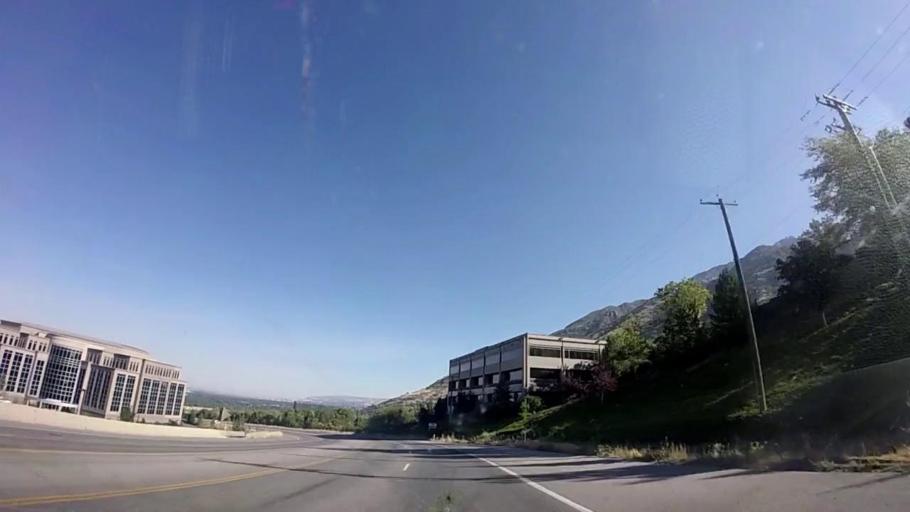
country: US
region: Utah
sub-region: Salt Lake County
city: Cottonwood Heights
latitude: 40.6329
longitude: -111.8000
